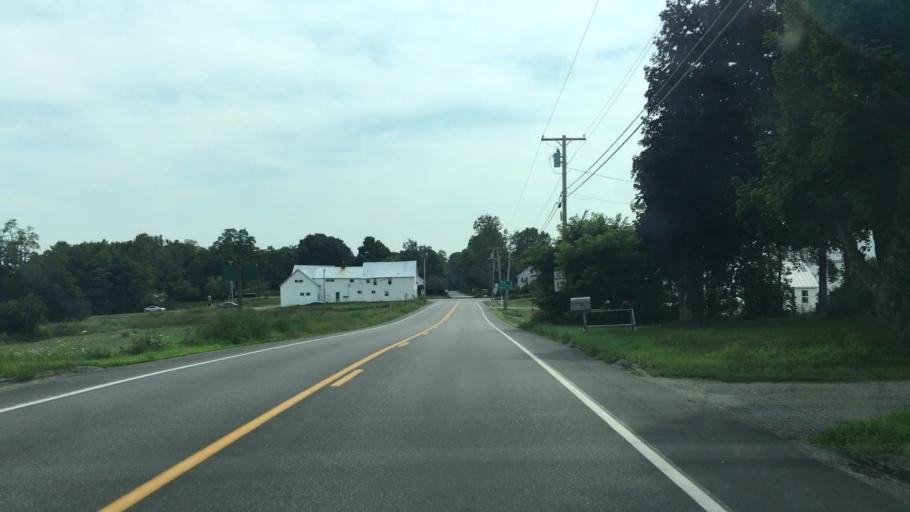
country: US
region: Maine
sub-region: Kennebec County
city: Windsor
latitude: 44.2808
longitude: -69.5973
